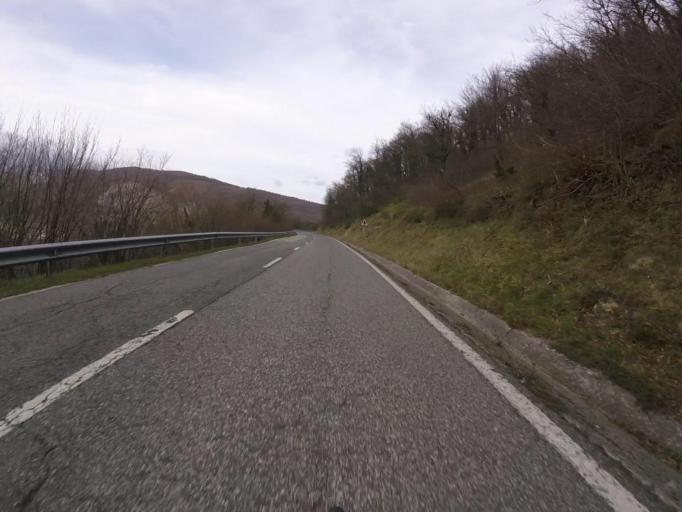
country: ES
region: Navarre
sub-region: Provincia de Navarra
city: Olazagutia
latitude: 42.8728
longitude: -2.1828
